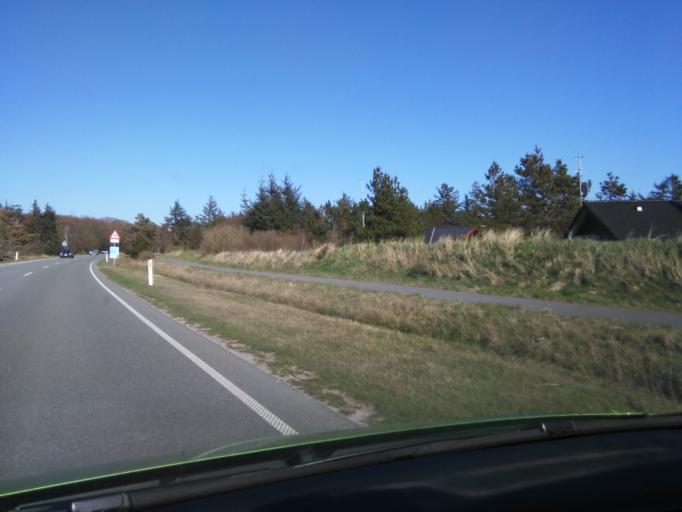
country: DK
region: South Denmark
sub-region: Varde Kommune
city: Oksbol
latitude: 55.5629
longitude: 8.1699
